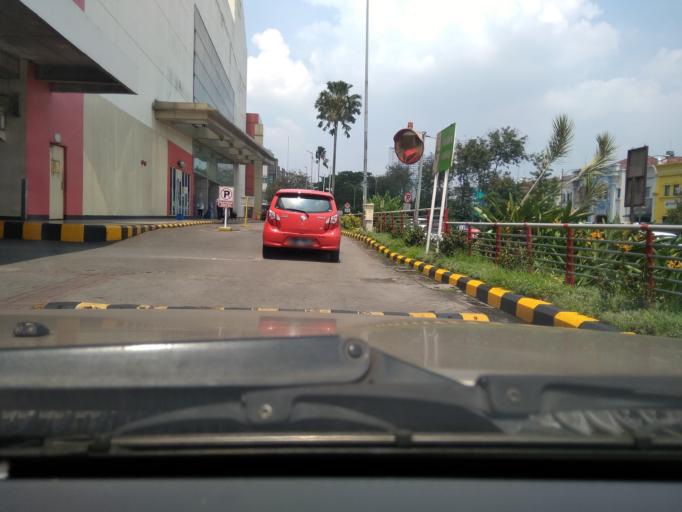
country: ID
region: West Java
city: Serpong
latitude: -6.2864
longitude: 106.6636
